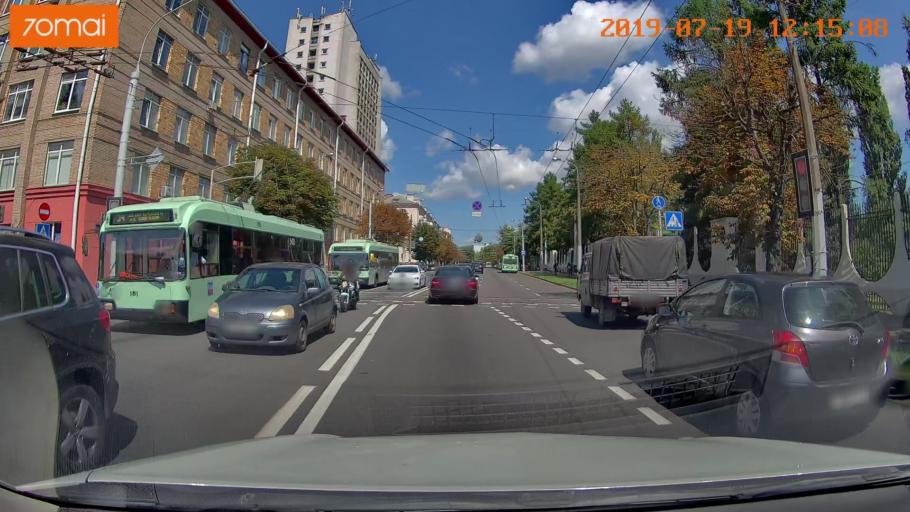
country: BY
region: Minsk
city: Minsk
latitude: 53.9156
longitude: 27.6039
